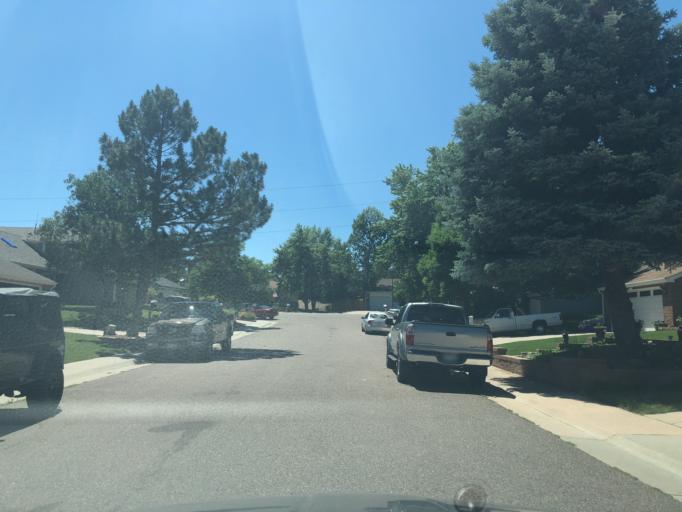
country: US
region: Colorado
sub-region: Arapahoe County
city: Dove Valley
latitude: 39.6166
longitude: -104.7902
